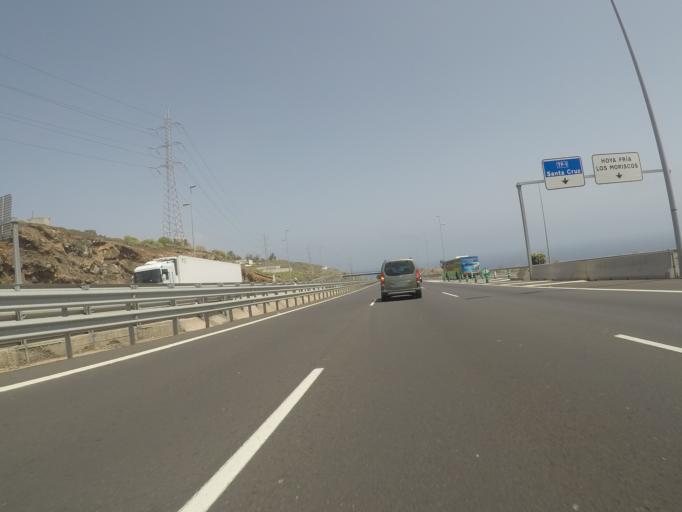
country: ES
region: Canary Islands
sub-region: Provincia de Santa Cruz de Tenerife
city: Santa Cruz de Tenerife
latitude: 28.4316
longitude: -16.2952
